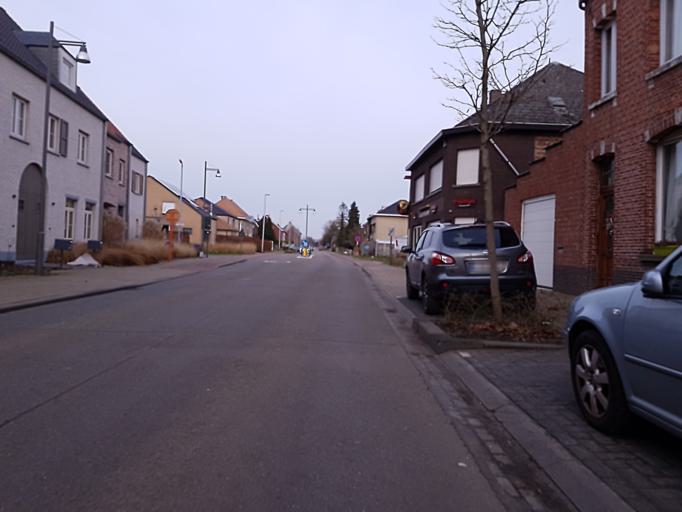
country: BE
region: Flanders
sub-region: Provincie Vlaams-Brabant
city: Tremelo
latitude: 51.0295
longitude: 4.6948
